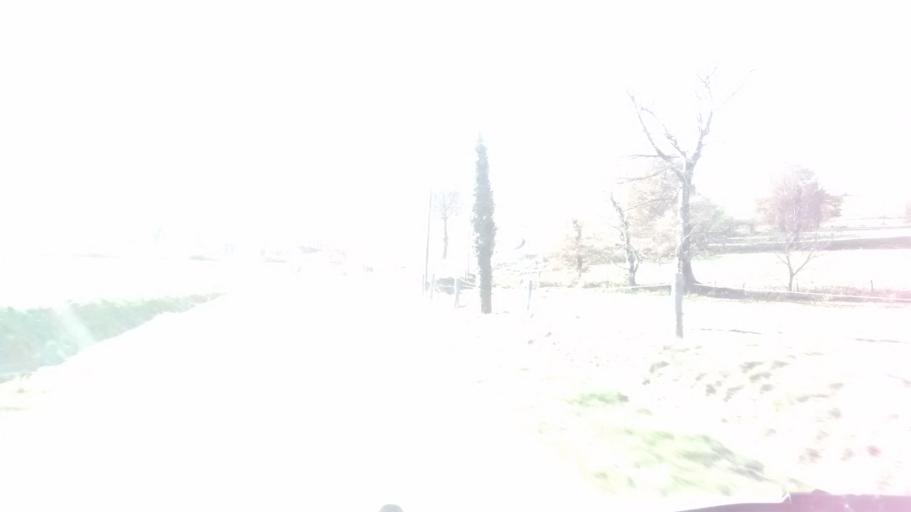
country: FR
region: Brittany
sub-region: Departement d'Ille-et-Vilaine
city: La Bouexiere
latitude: 48.2044
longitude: -1.4589
